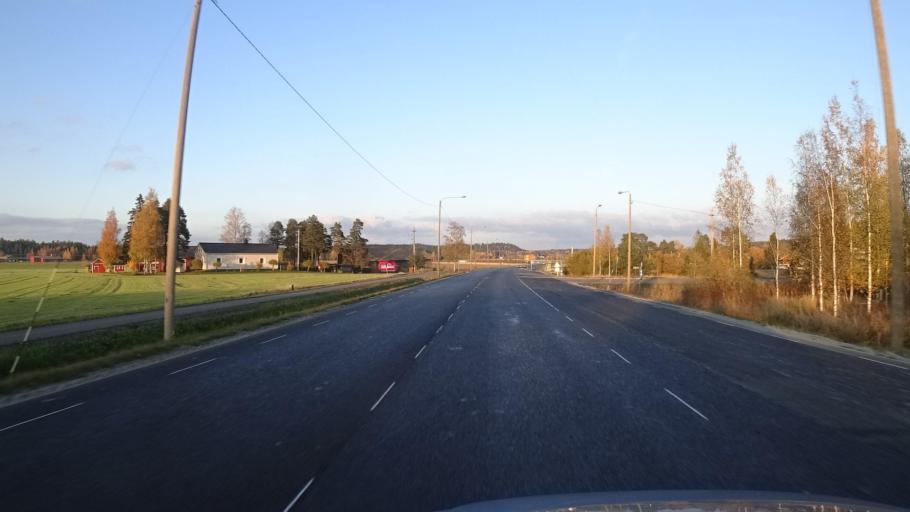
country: FI
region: Haeme
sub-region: Forssa
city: Forssa
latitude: 60.8202
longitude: 23.5508
